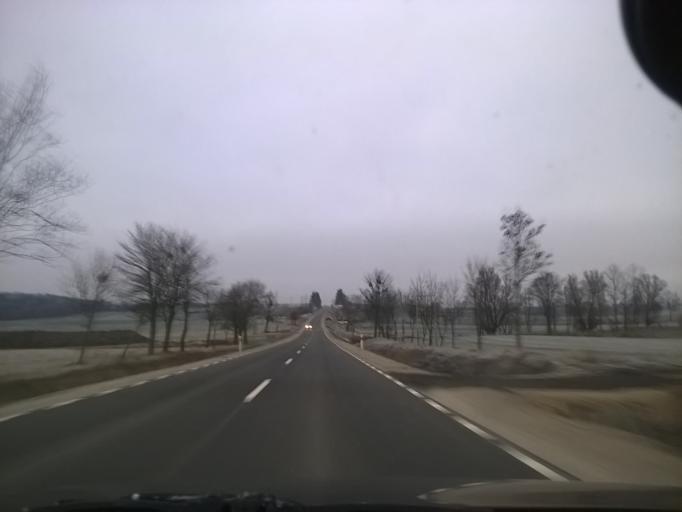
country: PL
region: Warmian-Masurian Voivodeship
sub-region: Powiat ketrzynski
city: Ketrzyn
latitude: 54.0613
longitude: 21.3483
